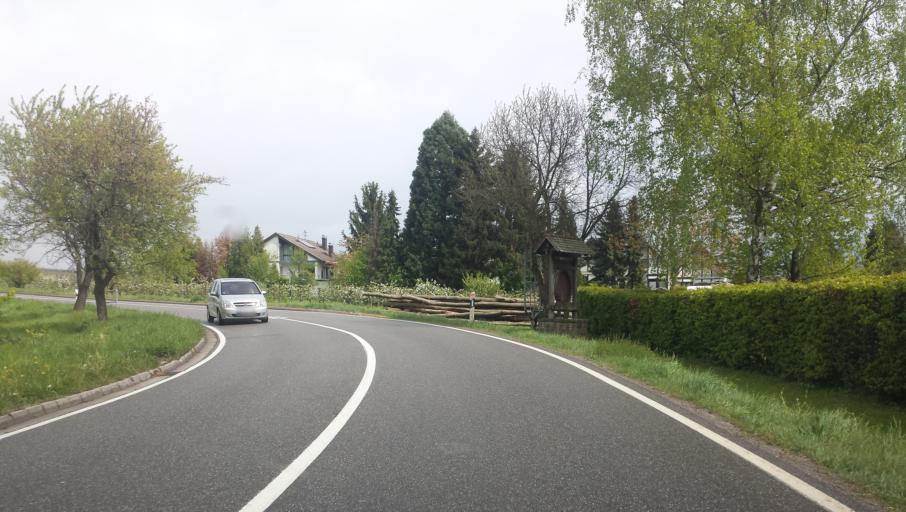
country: DE
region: Rheinland-Pfalz
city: Oberotterbach
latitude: 49.0723
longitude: 7.9715
